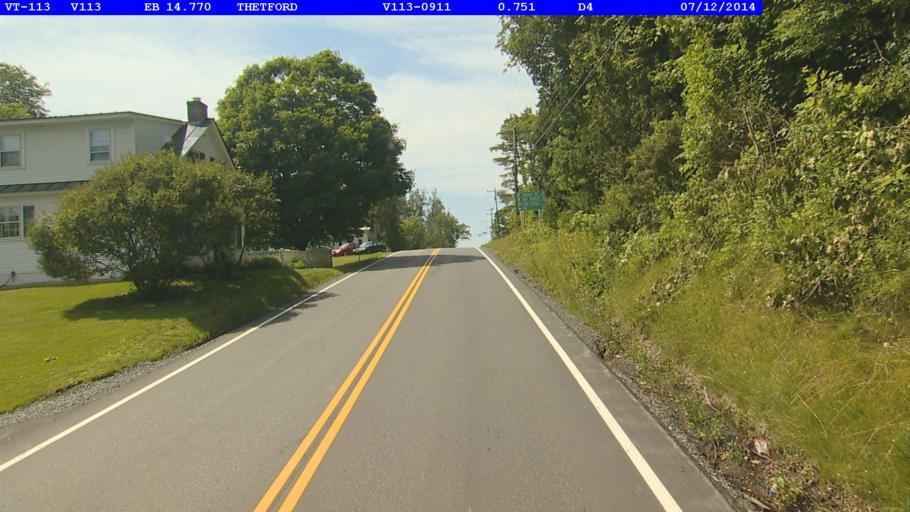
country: US
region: New Hampshire
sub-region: Grafton County
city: Orford
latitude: 43.8871
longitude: -72.2602
